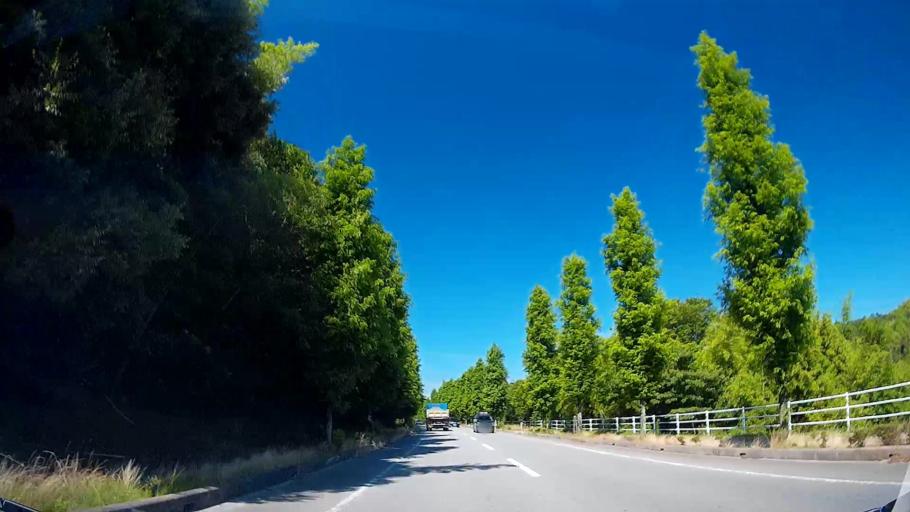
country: JP
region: Aichi
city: Gamagori
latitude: 34.8308
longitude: 137.1529
